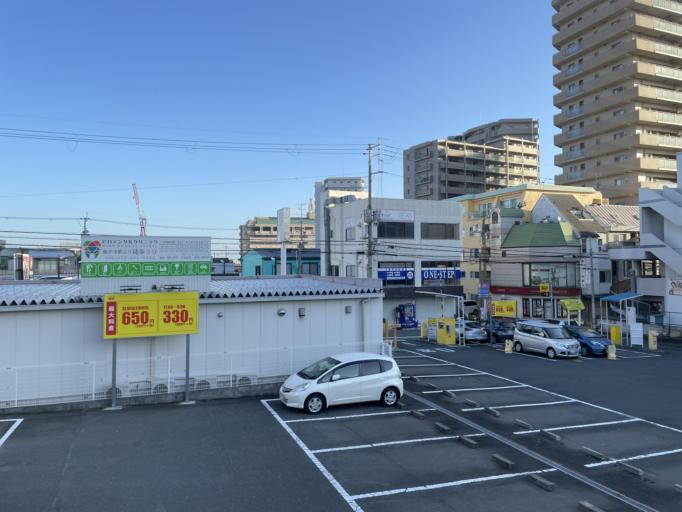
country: JP
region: Osaka
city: Kashihara
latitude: 34.5715
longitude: 135.5968
